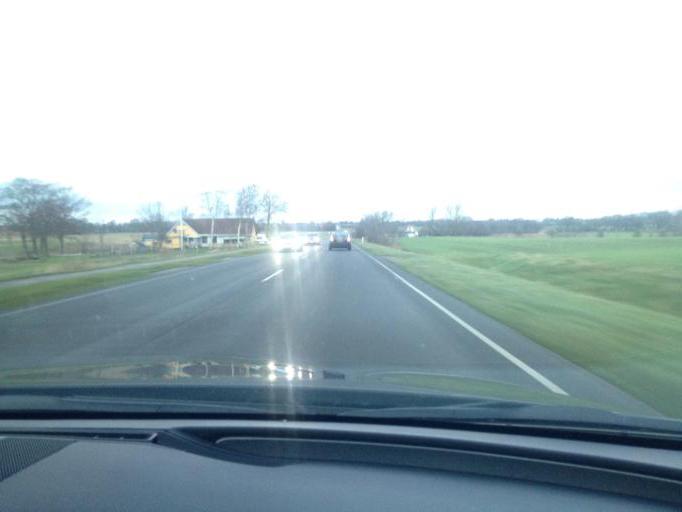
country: DK
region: South Denmark
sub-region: Kolding Kommune
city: Kolding
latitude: 55.5507
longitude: 9.4811
